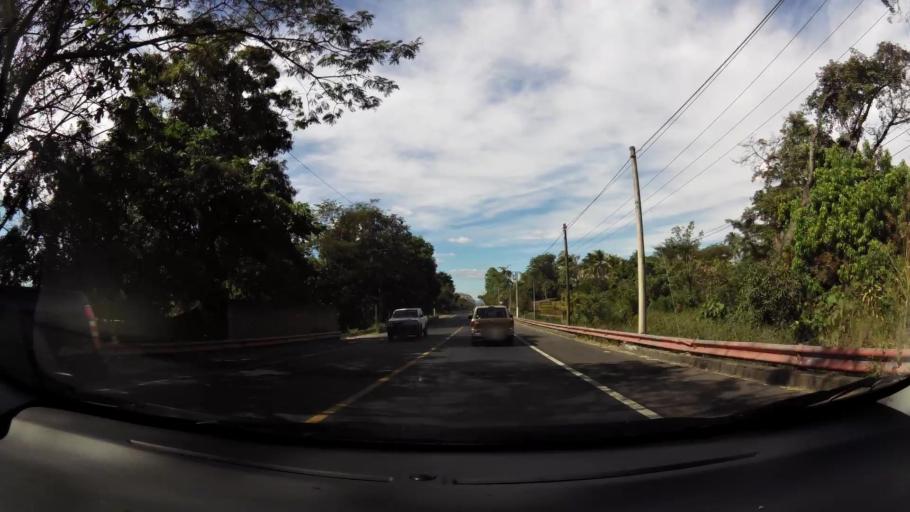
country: SV
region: San Salvador
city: Guazapa
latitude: 13.8594
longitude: -89.1635
